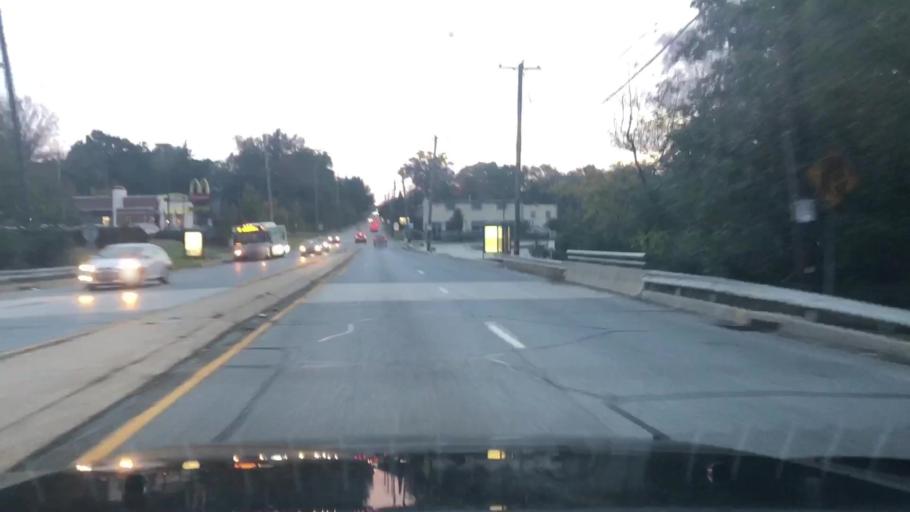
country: US
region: Pennsylvania
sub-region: Montgomery County
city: Norristown
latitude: 40.1427
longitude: -75.3118
